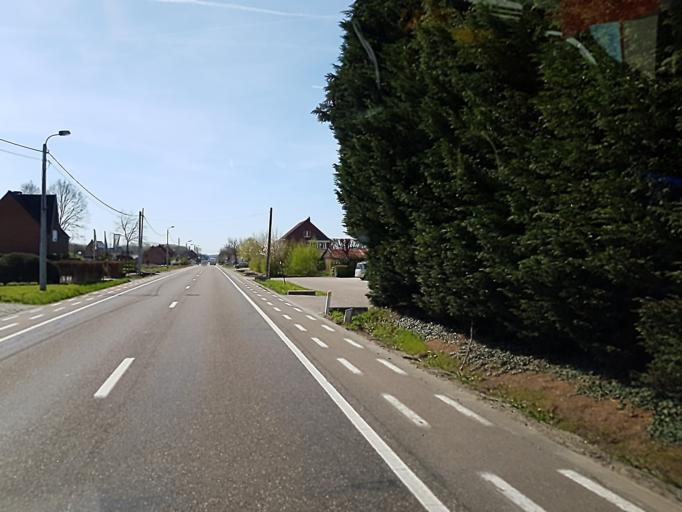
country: BE
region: Flanders
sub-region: Provincie Vlaams-Brabant
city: Aarschot
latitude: 51.0211
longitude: 4.8434
